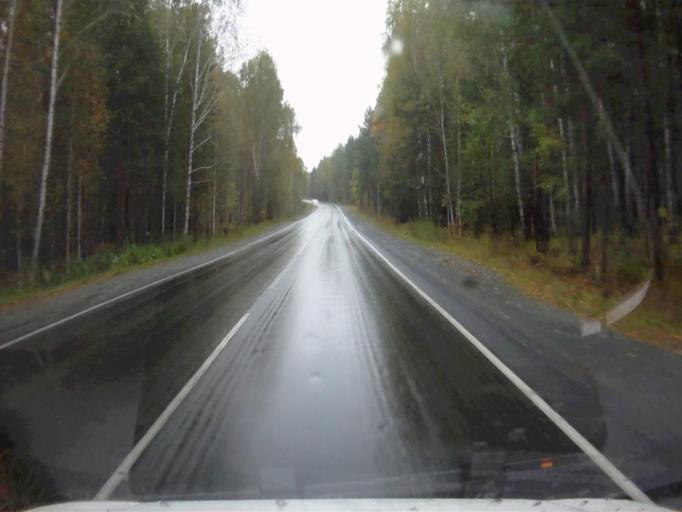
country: RU
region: Chelyabinsk
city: Tayginka
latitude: 55.5918
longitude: 60.6264
